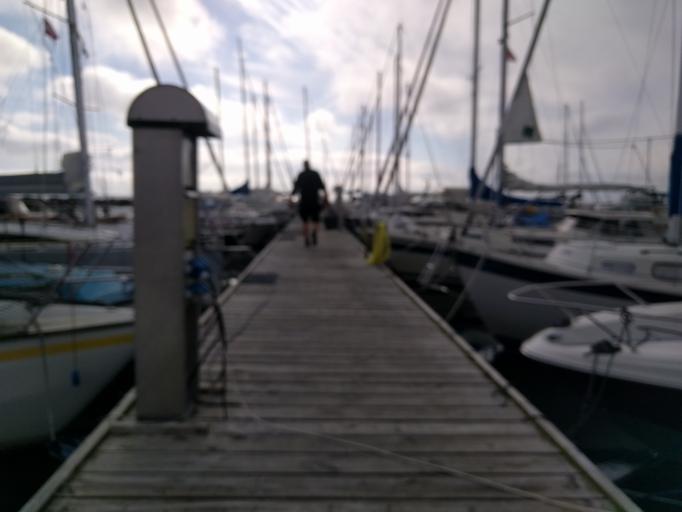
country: DK
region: South Denmark
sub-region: Kerteminde Kommune
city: Kerteminde
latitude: 55.4545
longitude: 10.6661
